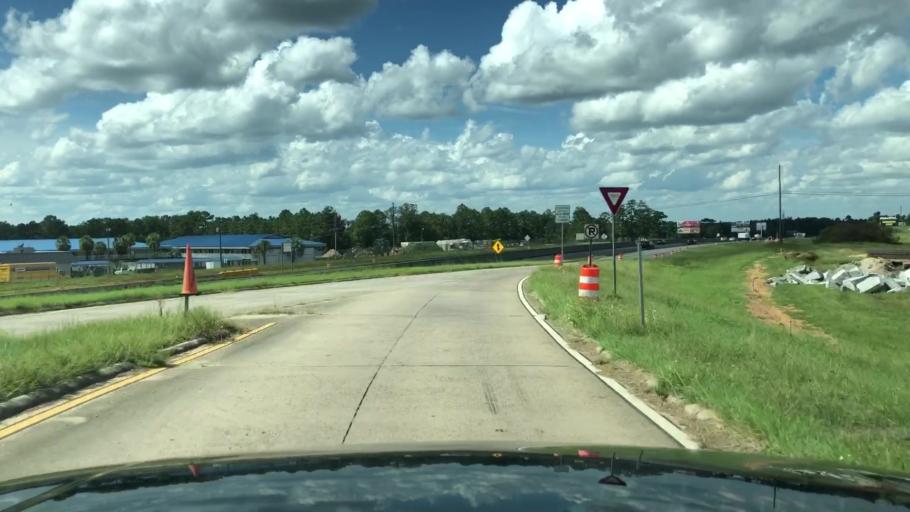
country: US
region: Georgia
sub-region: Lowndes County
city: Remerton
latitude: 30.8953
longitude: -83.3554
